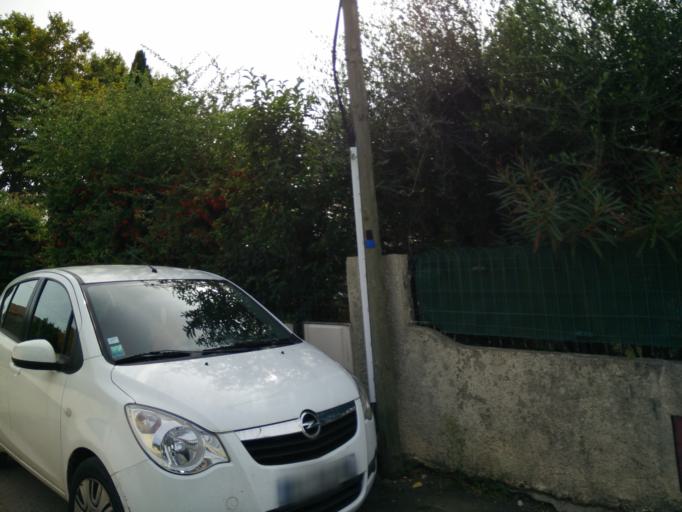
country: FR
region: Languedoc-Roussillon
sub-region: Departement du Gard
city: Caveirac
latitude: 43.8250
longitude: 4.2591
